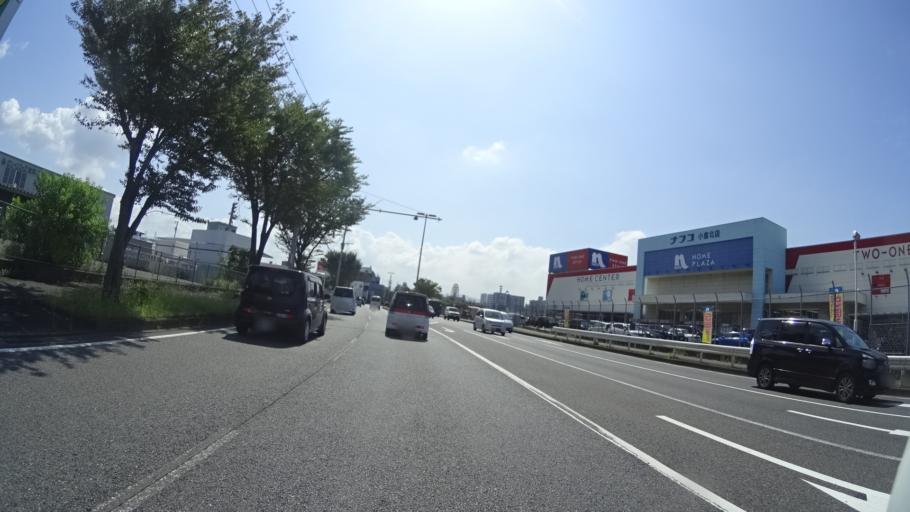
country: JP
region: Yamaguchi
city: Shimonoseki
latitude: 33.8888
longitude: 130.8960
